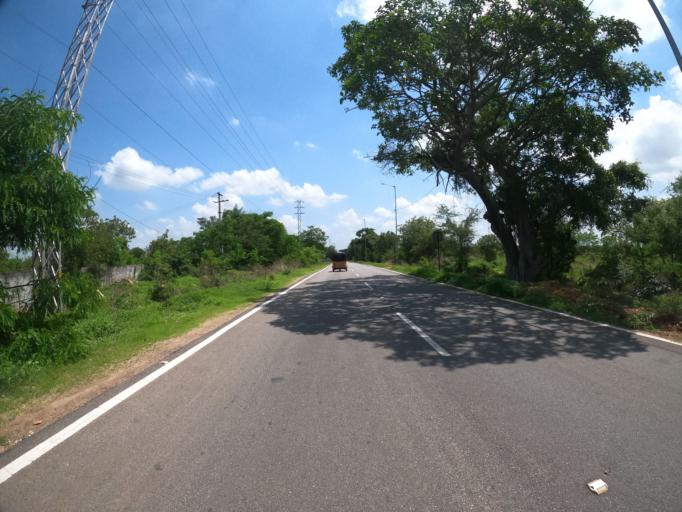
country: IN
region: Telangana
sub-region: Rangareddi
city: Sriramnagar
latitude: 17.3590
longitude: 78.3227
